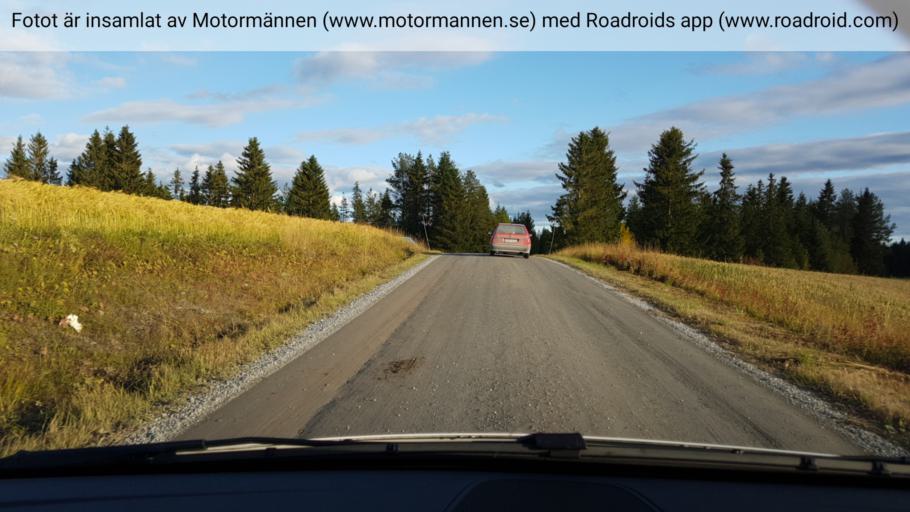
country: SE
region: Jaemtland
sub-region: Bergs Kommun
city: Hoverberg
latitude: 63.0333
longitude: 14.3496
